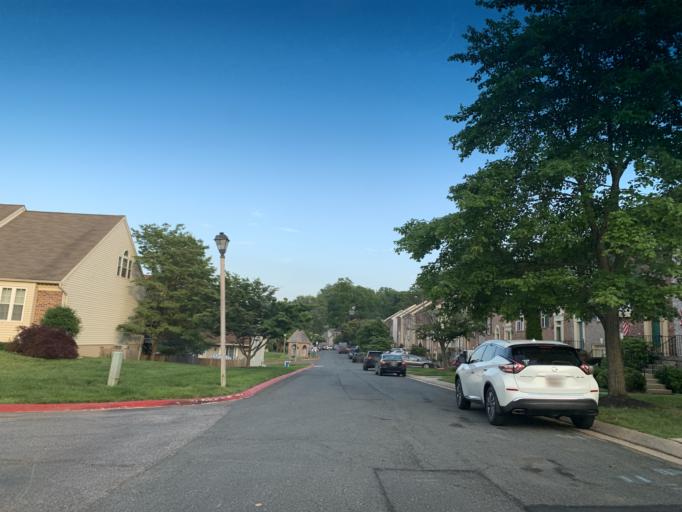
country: US
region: Maryland
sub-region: Harford County
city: North Bel Air
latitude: 39.5498
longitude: -76.3575
